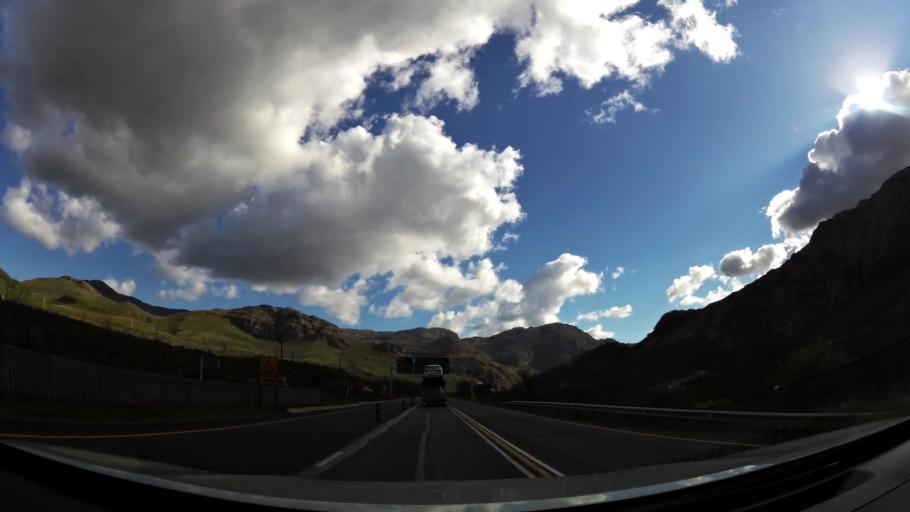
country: ZA
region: Western Cape
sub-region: Cape Winelands District Municipality
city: Paarl
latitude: -33.7270
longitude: 19.1386
